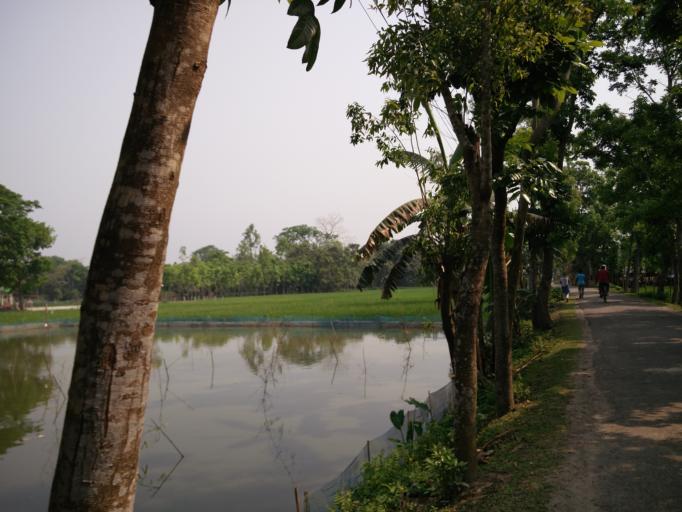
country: BD
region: Dhaka
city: Muktagacha
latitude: 24.9281
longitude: 90.2507
